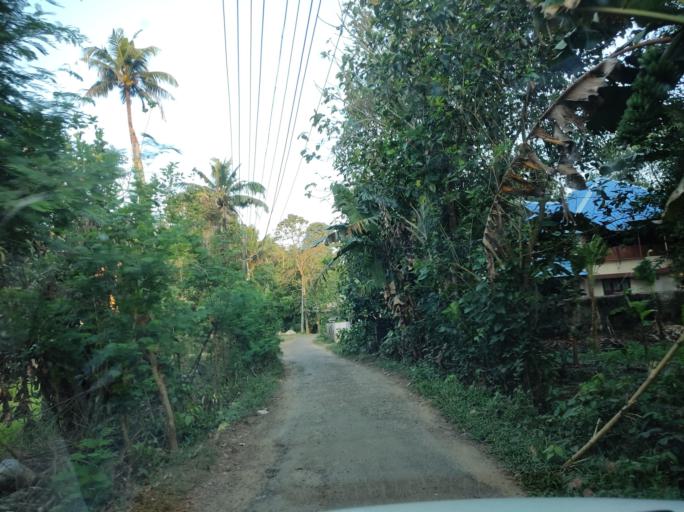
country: IN
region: Kerala
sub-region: Pattanamtitta
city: Tiruvalla
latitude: 9.3609
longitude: 76.5657
